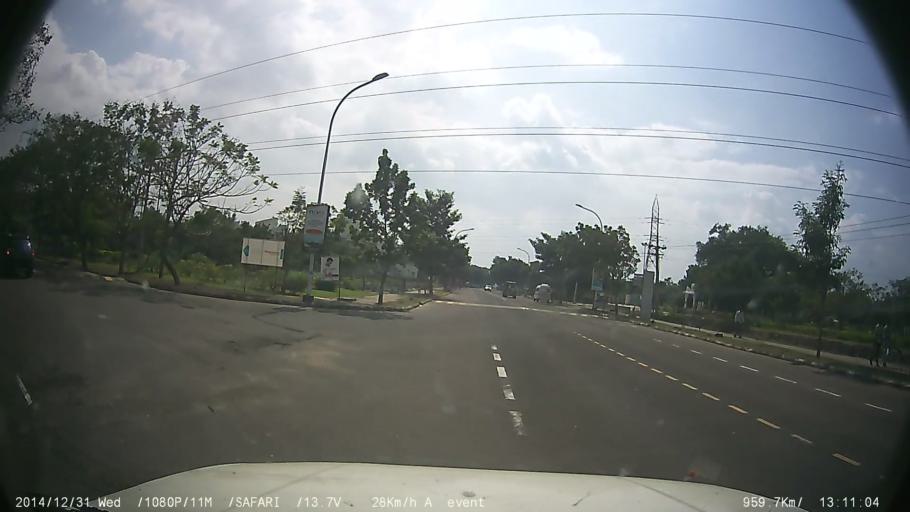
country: IN
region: Tamil Nadu
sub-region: Kancheepuram
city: Singapperumalkovil
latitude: 12.7337
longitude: 80.0016
